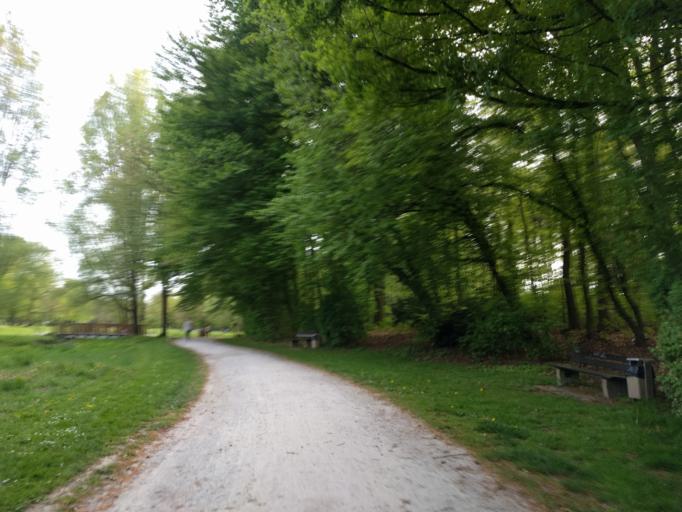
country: DE
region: North Rhine-Westphalia
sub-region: Regierungsbezirk Detmold
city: Bielefeld
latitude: 52.0512
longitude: 8.5325
